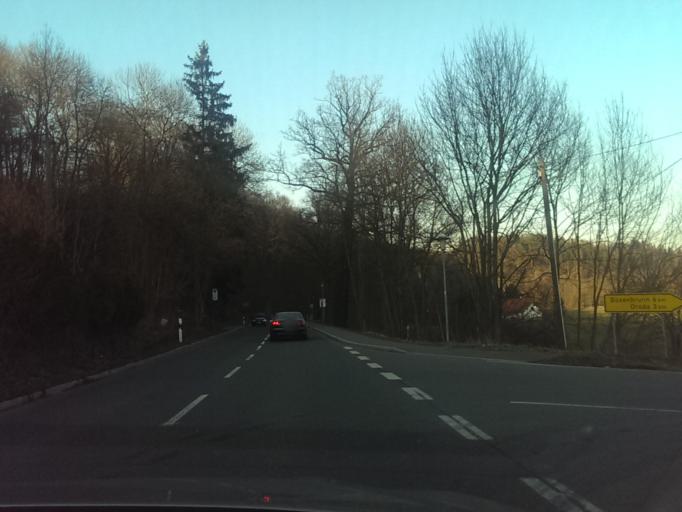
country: DE
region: Saxony
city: Weischlitz
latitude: 50.4246
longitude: 12.0669
